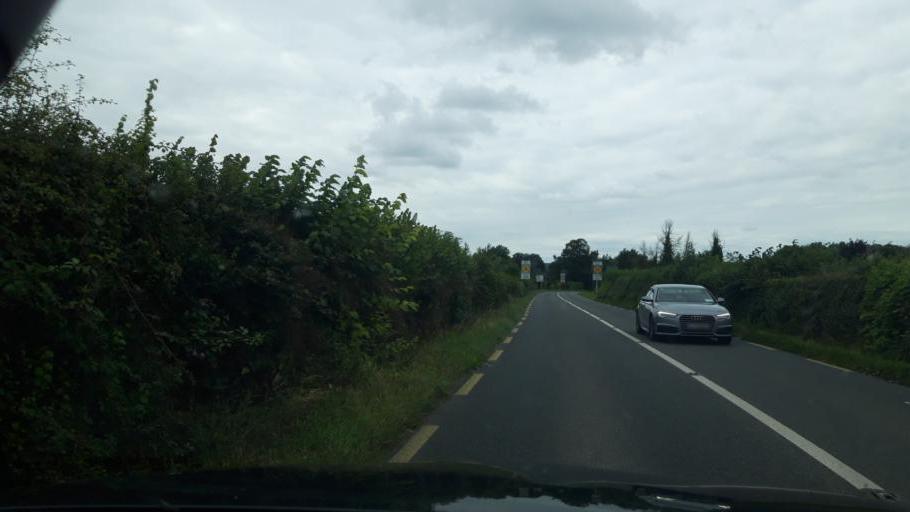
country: IE
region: Leinster
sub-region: Kilkenny
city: Thomastown
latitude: 52.6241
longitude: -7.0706
